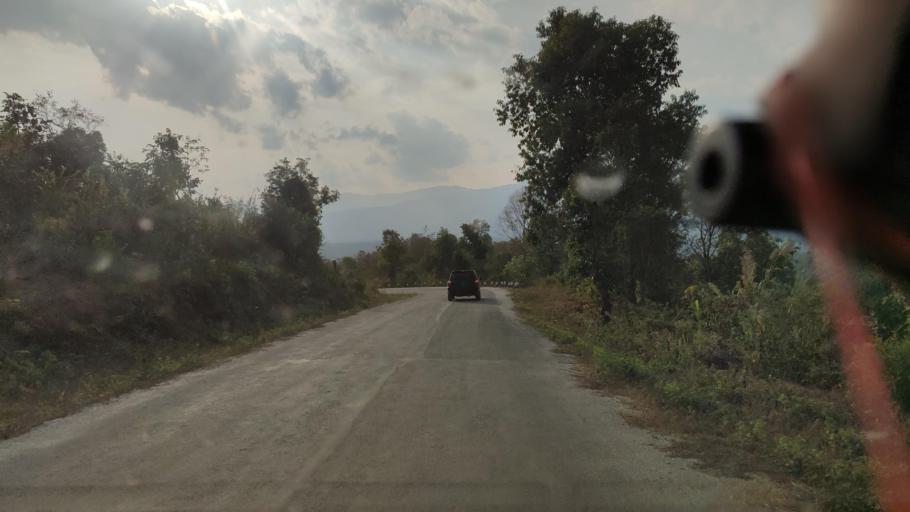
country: CN
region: Yunnan
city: Nayun
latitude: 21.4473
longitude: 99.6461
